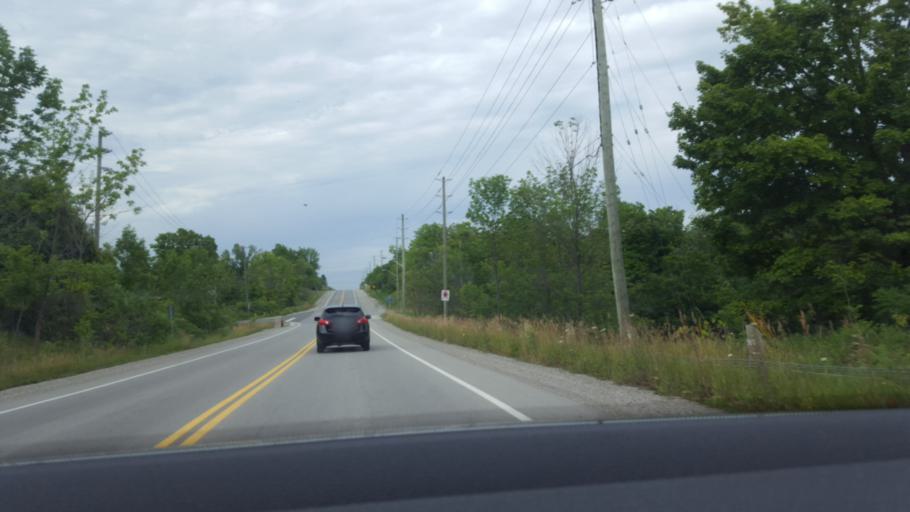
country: CA
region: Ontario
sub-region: Halton
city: Milton
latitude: 43.5150
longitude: -79.9502
